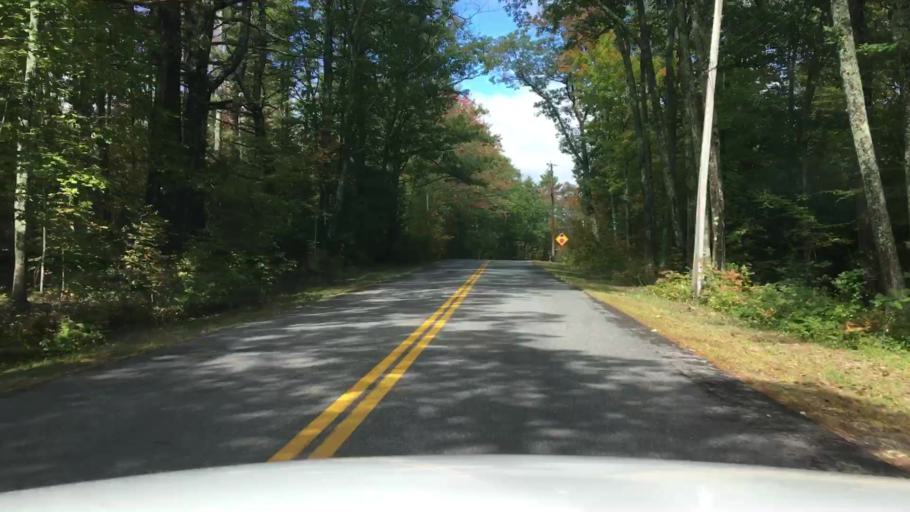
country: US
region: Maine
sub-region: Cumberland County
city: Brunswick
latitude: 43.9669
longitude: -69.8978
